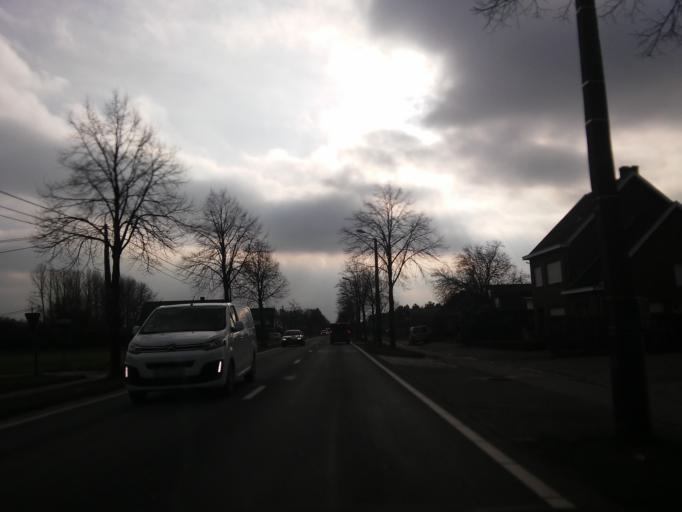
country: BE
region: Flanders
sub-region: Provincie Antwerpen
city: Olen
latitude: 51.1007
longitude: 4.8698
